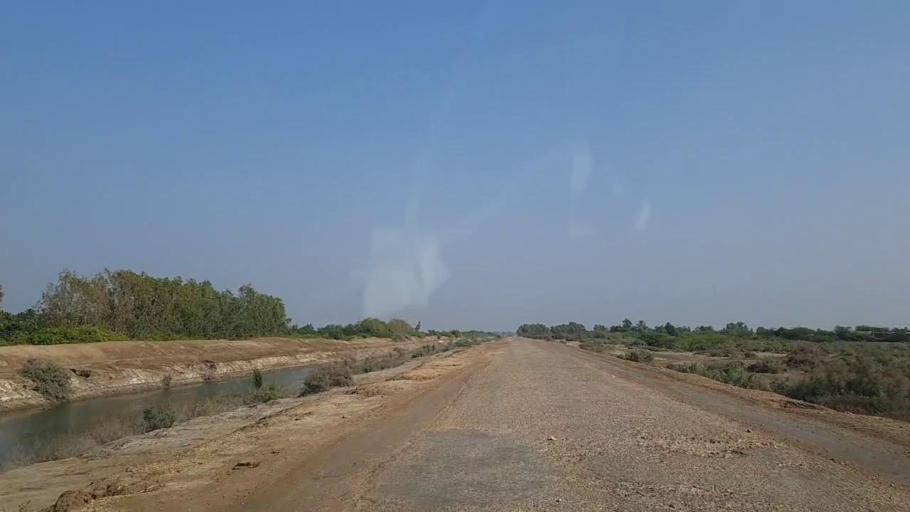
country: PK
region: Sindh
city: Mirpur Sakro
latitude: 24.6327
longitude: 67.6229
